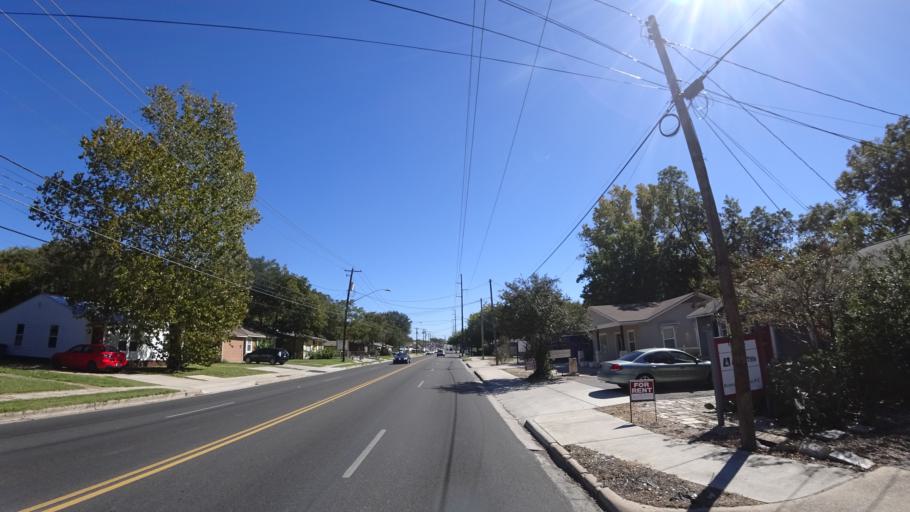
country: US
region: Texas
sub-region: Travis County
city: Austin
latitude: 30.3319
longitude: -97.7340
